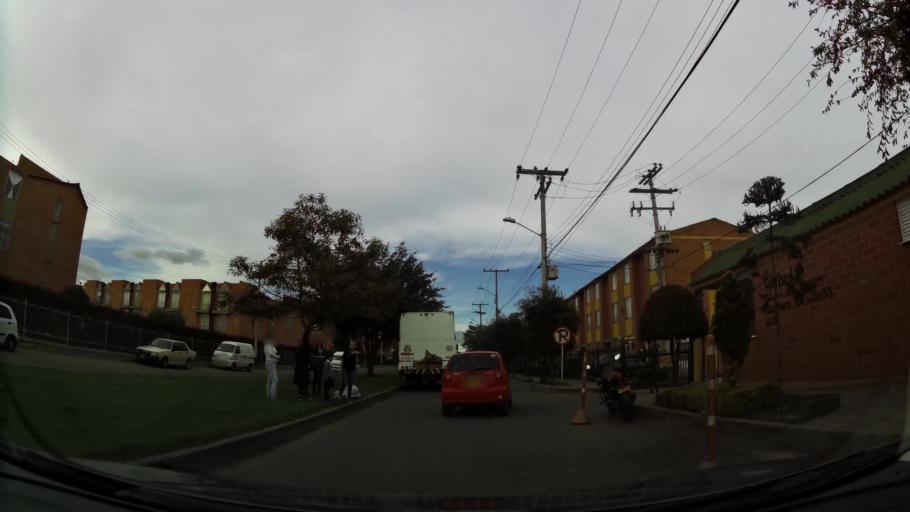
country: CO
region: Cundinamarca
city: Mosquera
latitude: 4.7067
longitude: -74.2251
